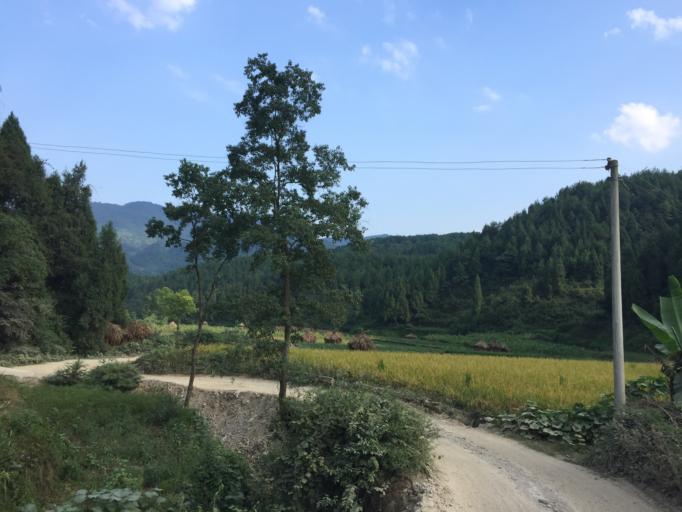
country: CN
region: Guizhou Sheng
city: Shiqian
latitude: 27.5995
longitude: 108.0268
